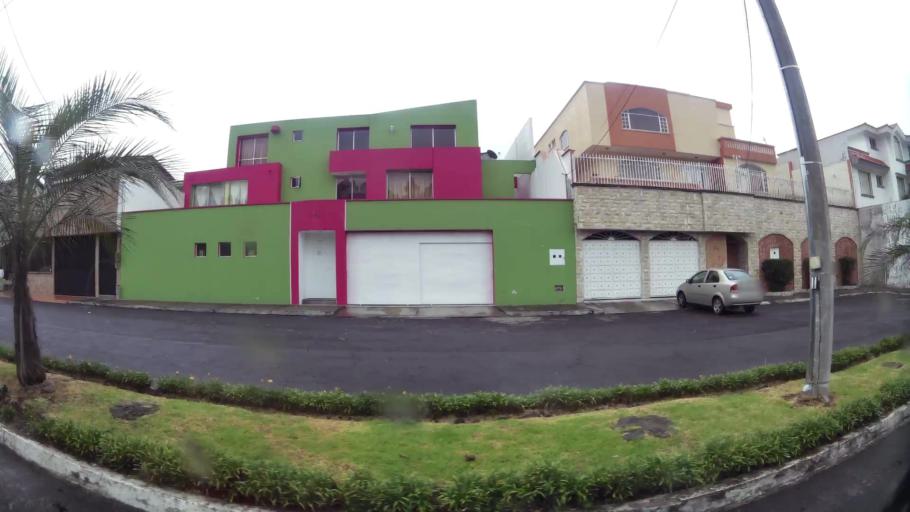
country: EC
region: Pichincha
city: Sangolqui
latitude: -0.3151
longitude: -78.4380
